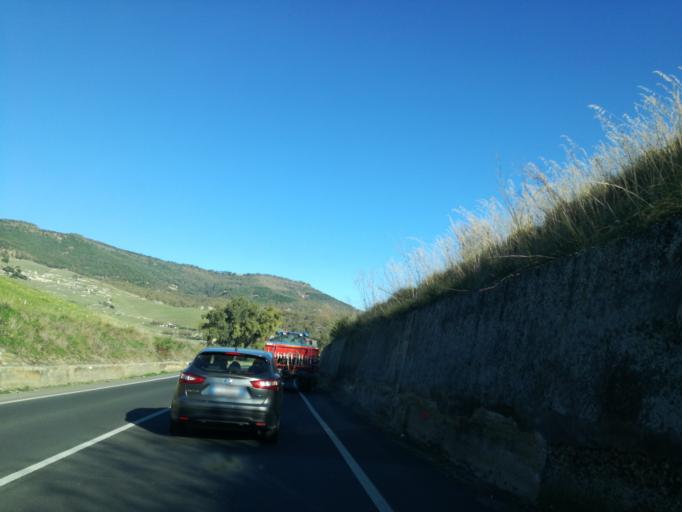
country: IT
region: Sicily
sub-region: Catania
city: San Michele di Ganzaria
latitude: 37.2371
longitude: 14.4501
